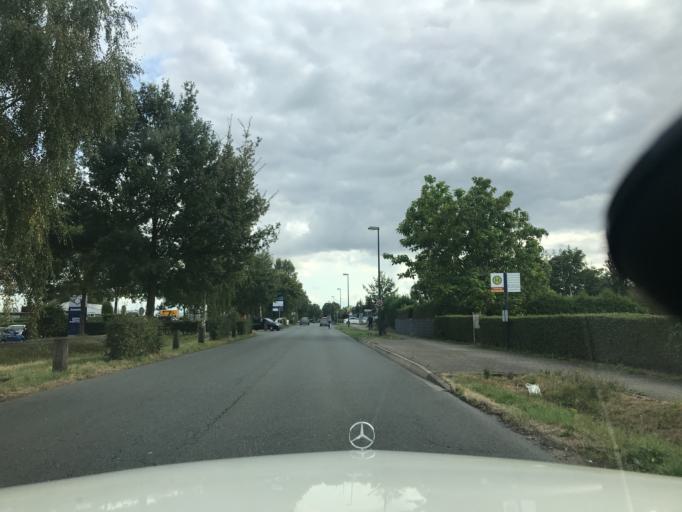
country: DE
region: North Rhine-Westphalia
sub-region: Regierungsbezirk Arnsberg
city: Lippstadt
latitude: 51.6559
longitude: 8.3559
